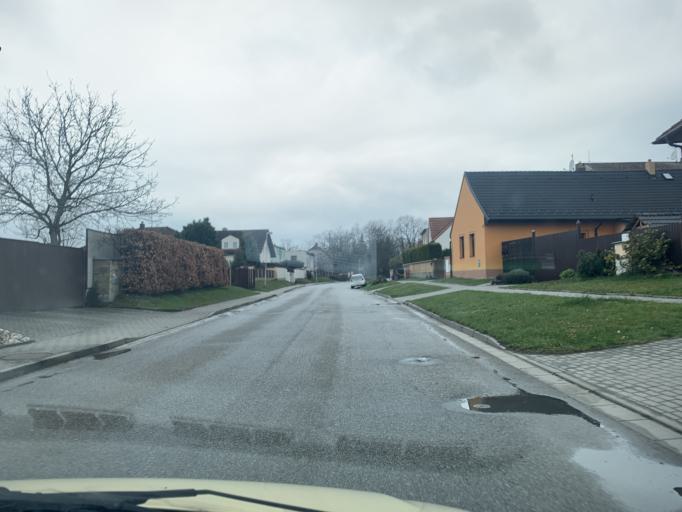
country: CZ
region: Jihocesky
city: Litvinovice
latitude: 48.9622
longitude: 14.4499
